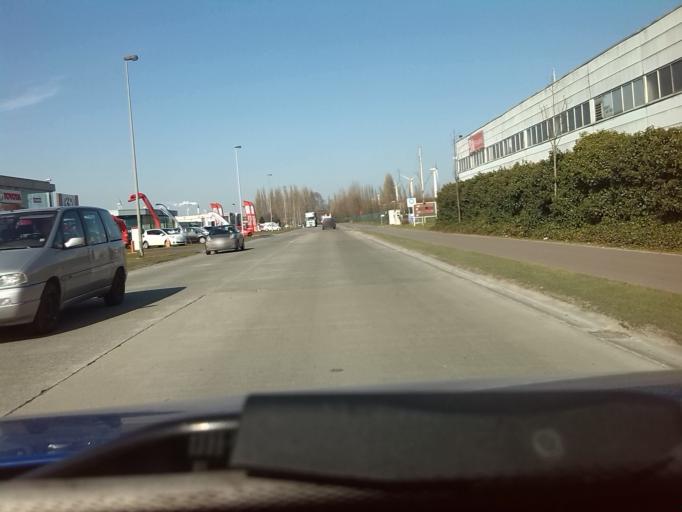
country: BE
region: Flanders
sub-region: Provincie West-Vlaanderen
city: Brugge
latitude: 51.2413
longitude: 3.2166
